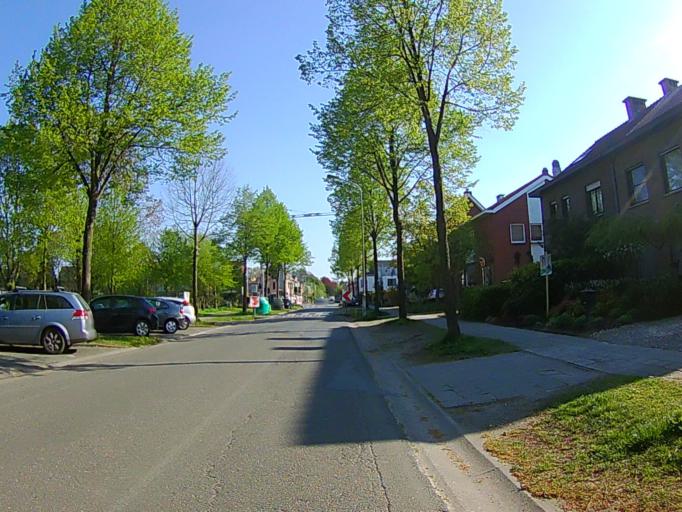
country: BE
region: Flanders
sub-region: Provincie Antwerpen
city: Schoten
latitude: 51.2526
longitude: 4.4823
